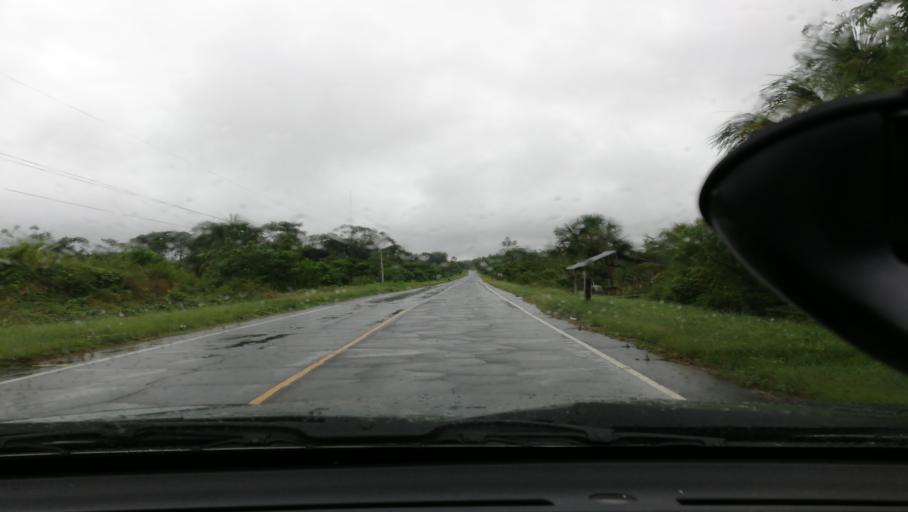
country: PE
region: Loreto
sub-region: Provincia de Maynas
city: San Juan
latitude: -4.1622
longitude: -73.4740
